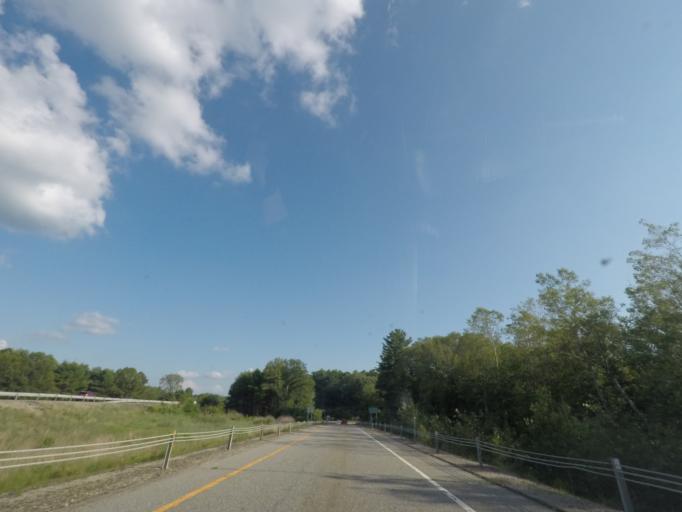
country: US
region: Massachusetts
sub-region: Worcester County
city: Webster
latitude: 42.0101
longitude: -71.8561
